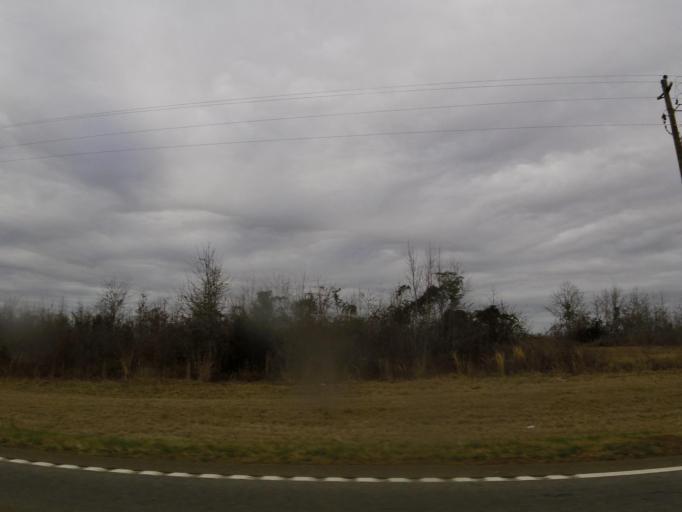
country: US
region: Georgia
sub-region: Randolph County
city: Shellman
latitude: 31.7729
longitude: -84.6766
